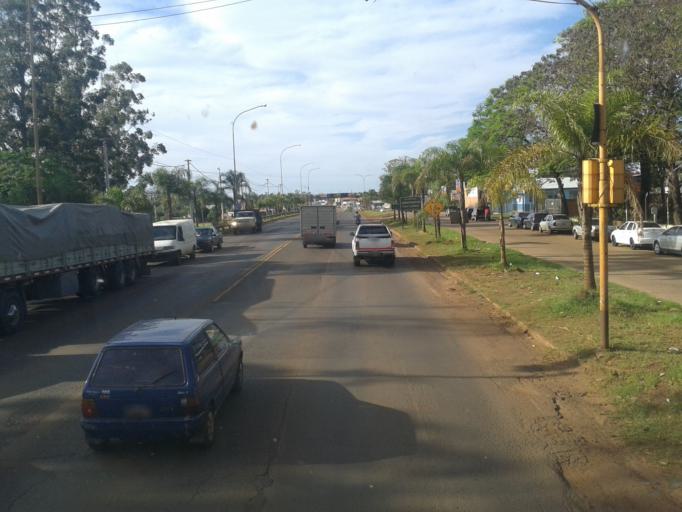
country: AR
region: Misiones
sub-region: Departamento de Capital
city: Posadas
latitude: -27.4141
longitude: -55.9011
